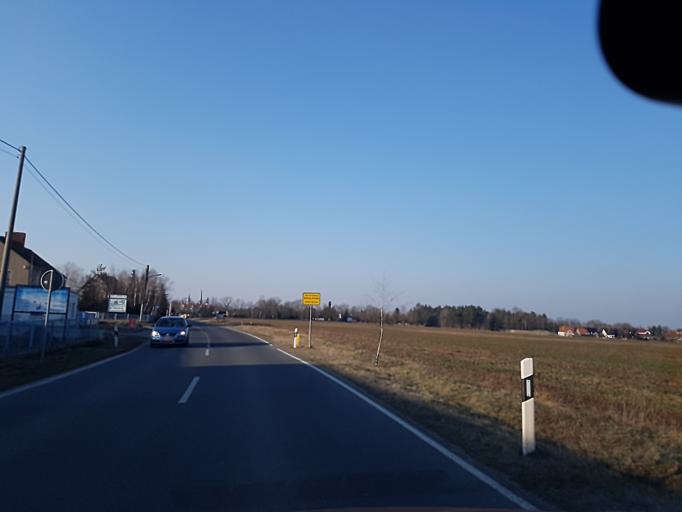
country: DE
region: Brandenburg
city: Ruckersdorf
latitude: 51.6027
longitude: 13.5515
